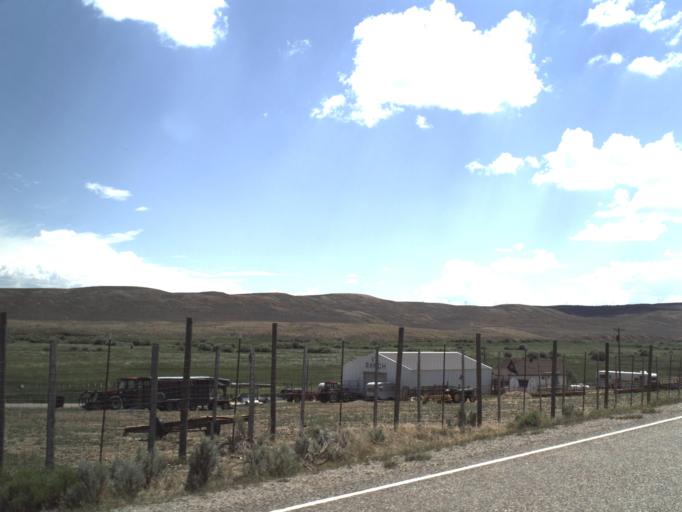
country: US
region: Utah
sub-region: Rich County
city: Randolph
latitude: 41.5176
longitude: -111.2092
